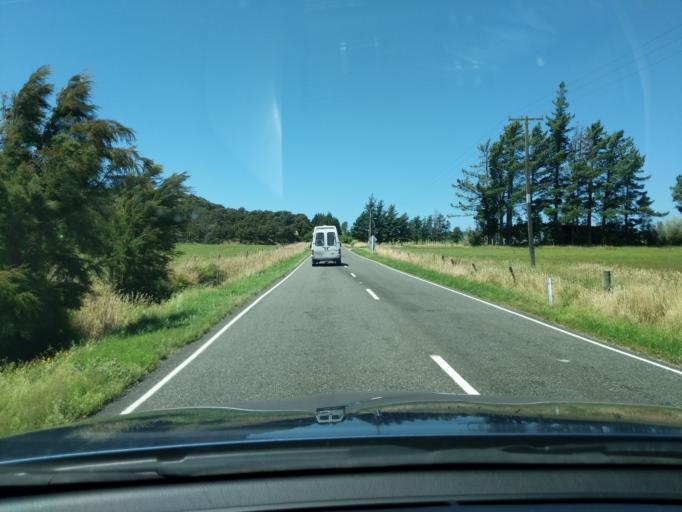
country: NZ
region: Tasman
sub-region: Tasman District
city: Takaka
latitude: -40.6947
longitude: 172.6363
